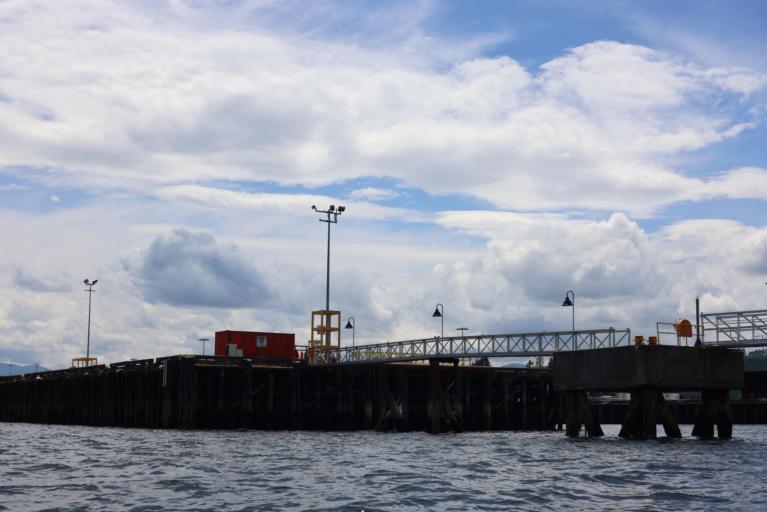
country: CA
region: British Columbia
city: Nanaimo
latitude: 49.1651
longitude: -123.9246
